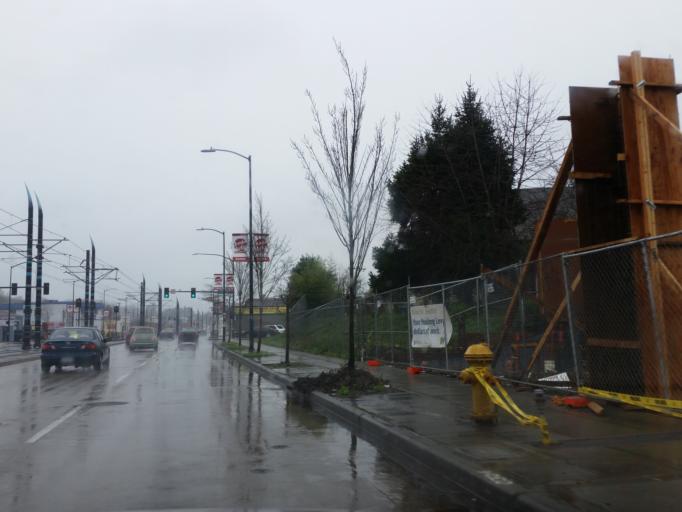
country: US
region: Washington
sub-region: King County
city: Riverton
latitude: 47.5399
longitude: -122.2824
